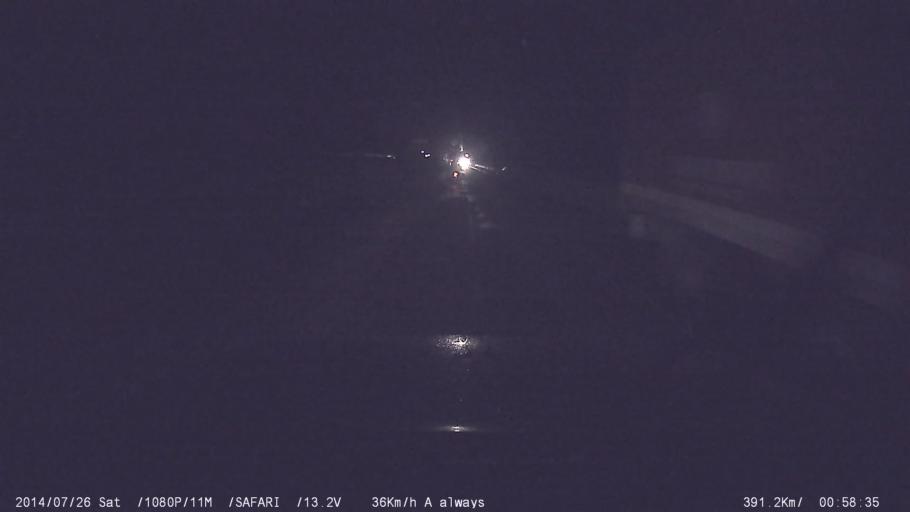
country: IN
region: Kerala
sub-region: Palakkad district
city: Palakkad
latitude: 10.7897
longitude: 76.7201
